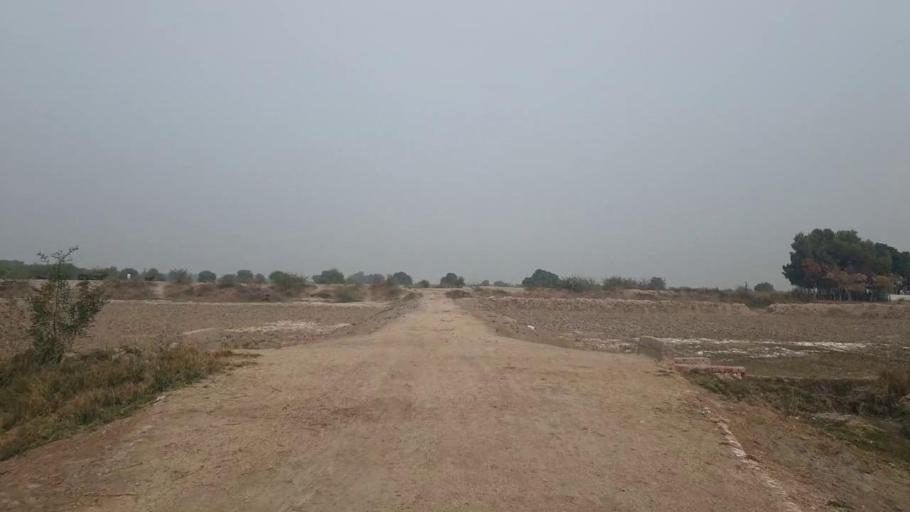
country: PK
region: Sindh
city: Tando Adam
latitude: 25.7880
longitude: 68.6649
